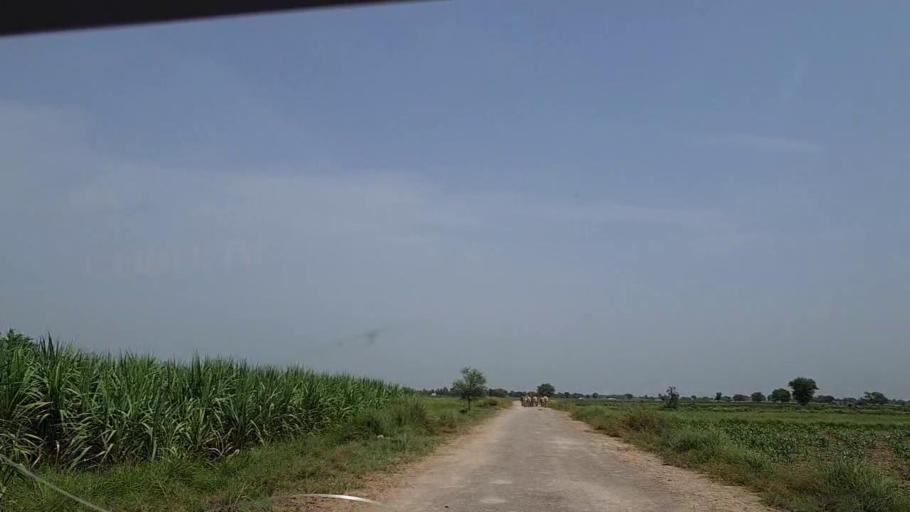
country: PK
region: Sindh
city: Tharu Shah
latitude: 26.9096
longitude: 68.0530
